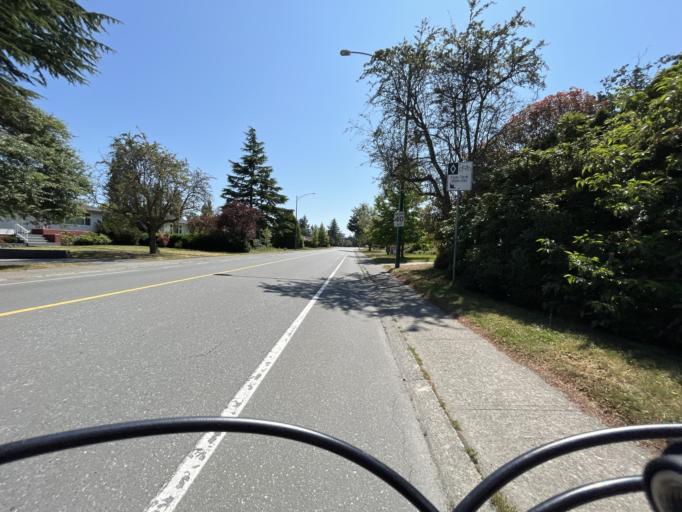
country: CA
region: British Columbia
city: Oak Bay
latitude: 48.4516
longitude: -123.3160
